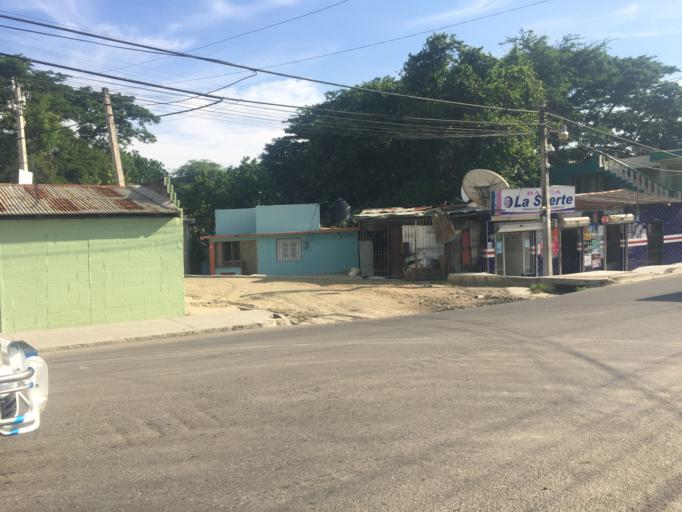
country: DO
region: Santiago
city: La Canela
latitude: 19.4527
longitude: -70.7625
